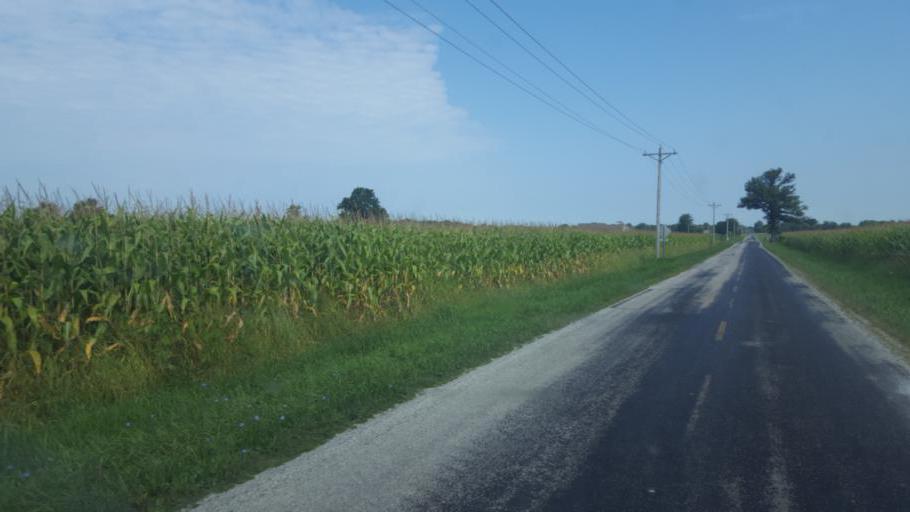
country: US
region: Ohio
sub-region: Morrow County
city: Cardington
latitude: 40.5147
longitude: -82.9955
